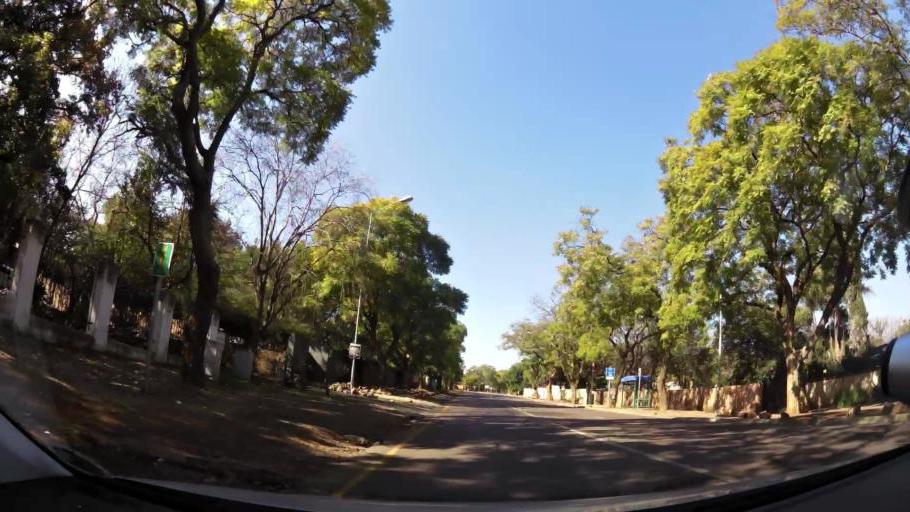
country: ZA
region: Gauteng
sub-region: City of Tshwane Metropolitan Municipality
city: Pretoria
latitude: -25.7644
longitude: 28.2257
